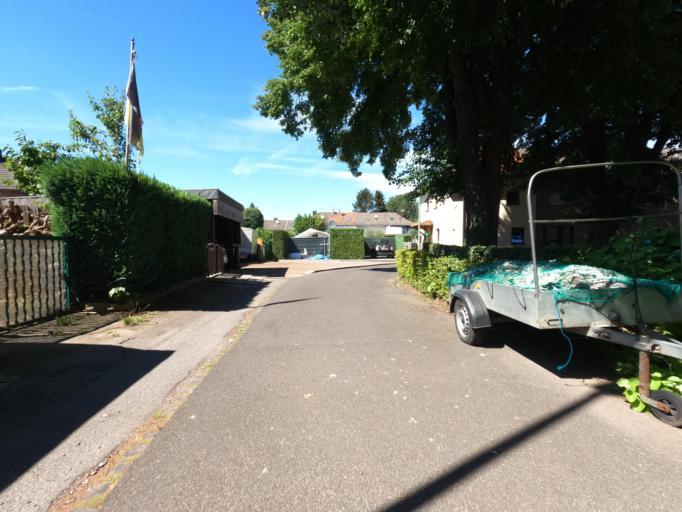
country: DE
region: North Rhine-Westphalia
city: Baesweiler
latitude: 50.9130
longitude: 6.1760
